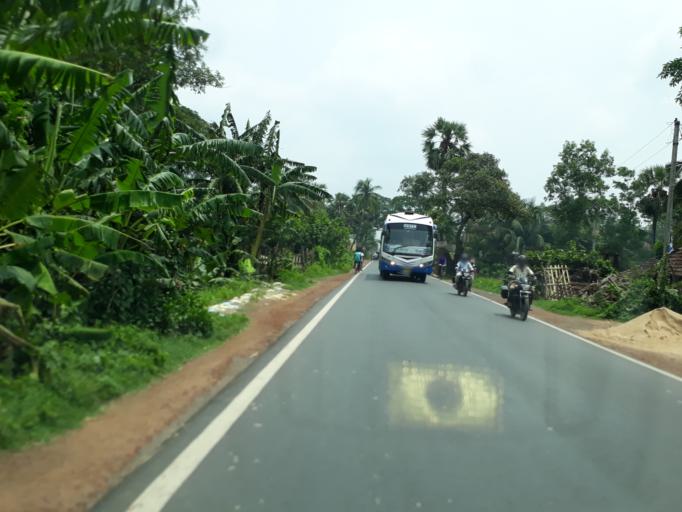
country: IN
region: West Bengal
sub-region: Purba Medinipur
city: Mahishadal
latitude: 22.1835
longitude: 87.9164
